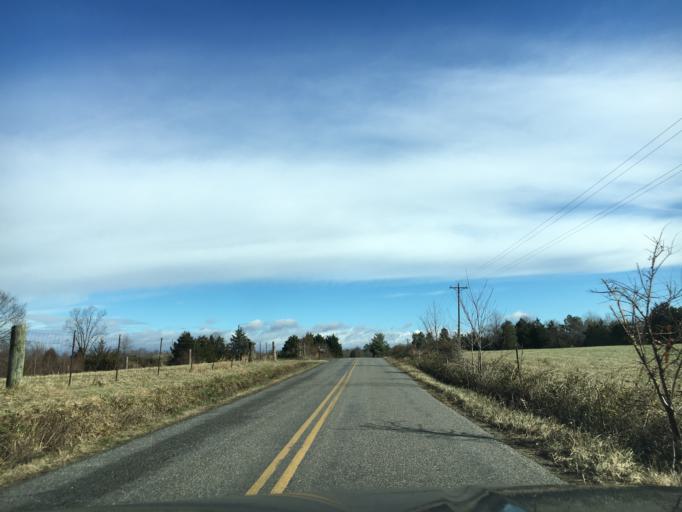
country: US
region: Virginia
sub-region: Amelia County
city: Amelia Court House
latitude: 37.3956
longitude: -78.1014
